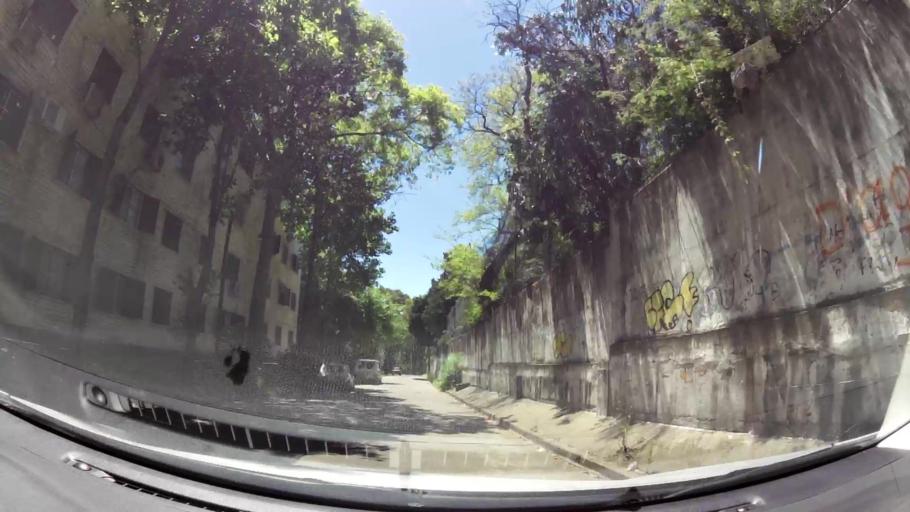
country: AR
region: Buenos Aires
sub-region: Partido de Tigre
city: Tigre
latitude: -34.4610
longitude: -58.5585
